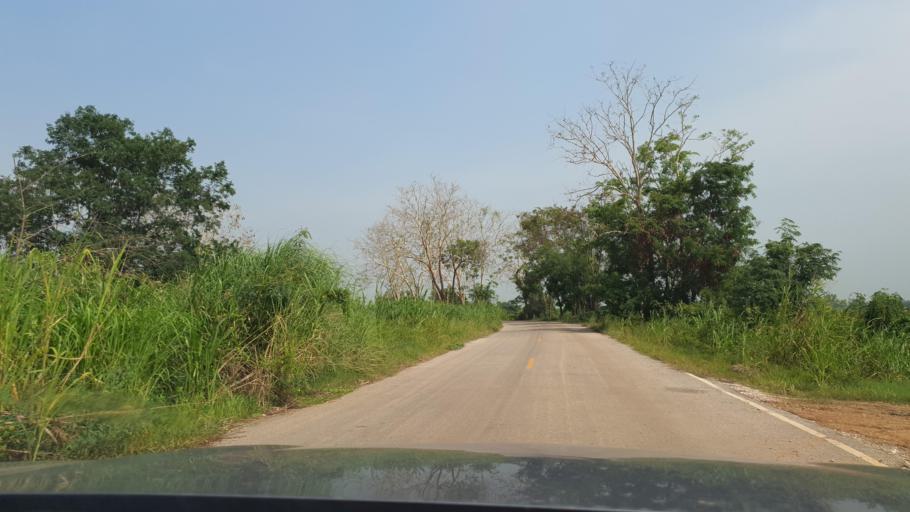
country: TH
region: Phitsanulok
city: Bang Rakam
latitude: 16.8022
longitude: 100.1160
